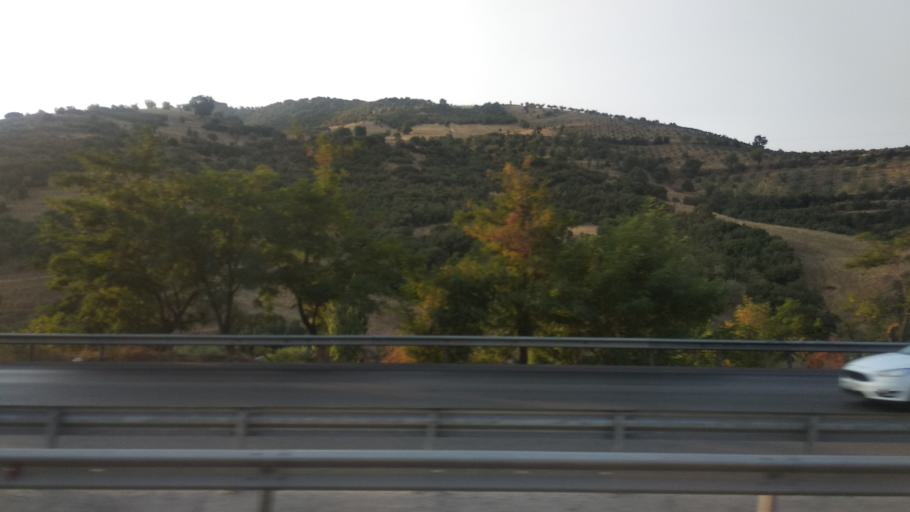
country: TR
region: Manisa
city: Menye
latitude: 38.5485
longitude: 28.4561
